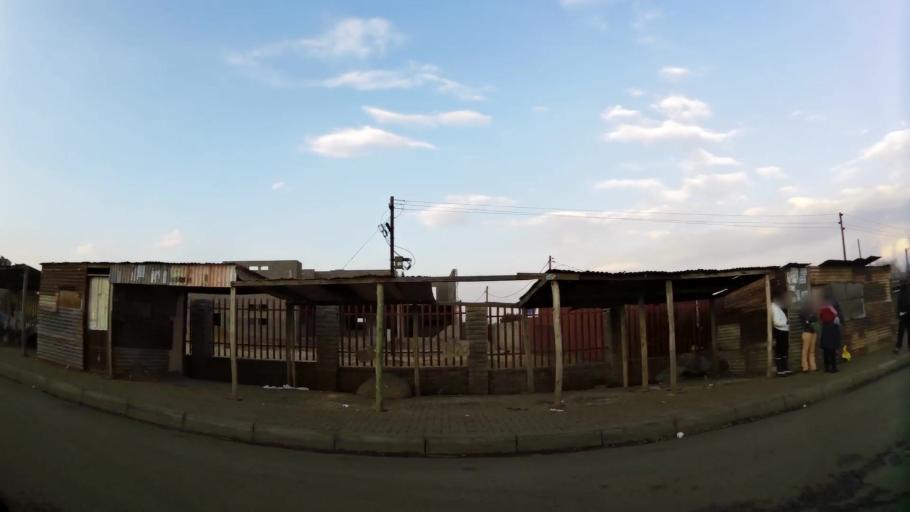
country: ZA
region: Gauteng
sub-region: City of Johannesburg Metropolitan Municipality
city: Orange Farm
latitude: -26.5382
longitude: 27.8323
